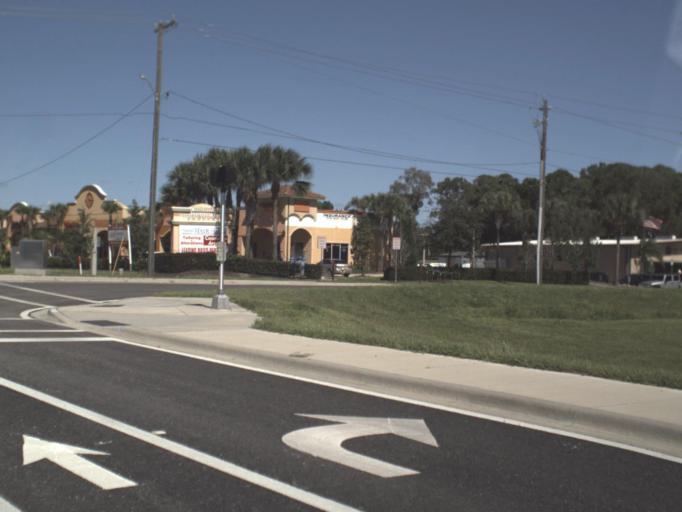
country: US
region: Florida
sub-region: Lee County
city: Estero
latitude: 26.4417
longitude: -81.8109
